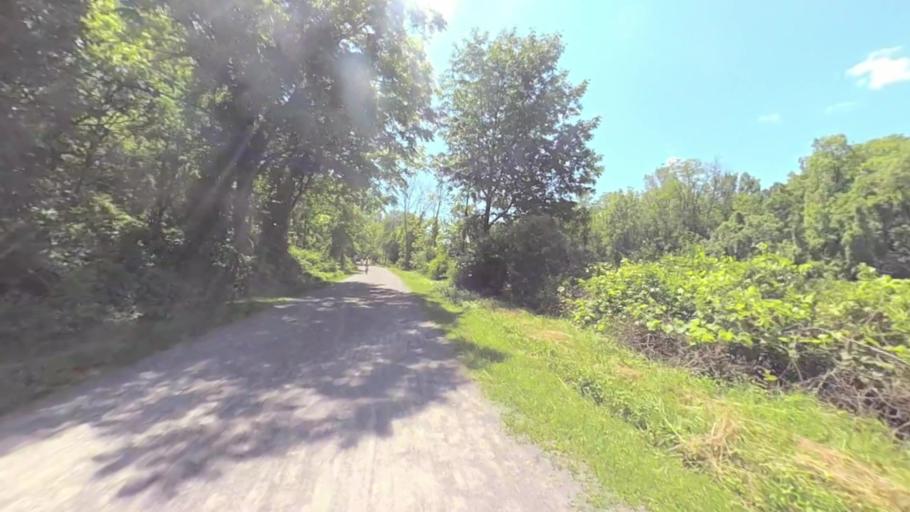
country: US
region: New York
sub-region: Monroe County
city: Pittsford
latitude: 43.0807
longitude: -77.5028
